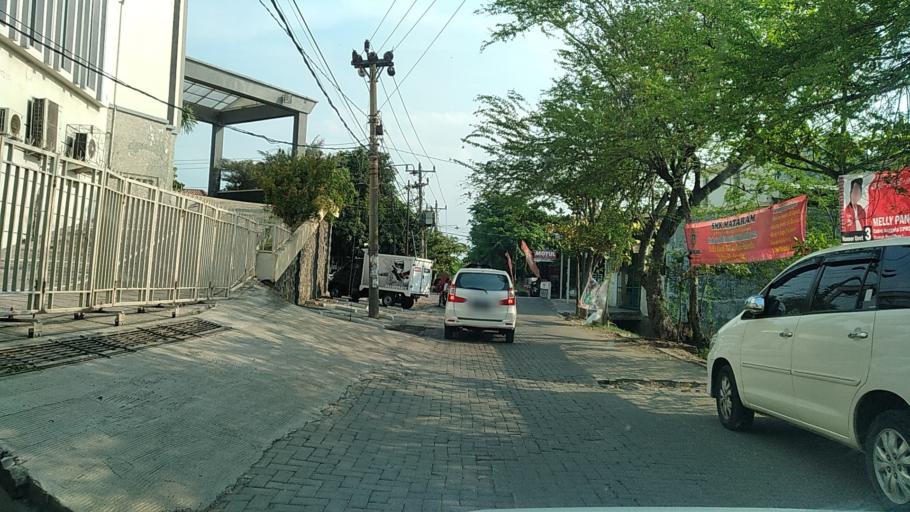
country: ID
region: Central Java
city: Semarang
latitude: -6.9547
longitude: 110.4041
